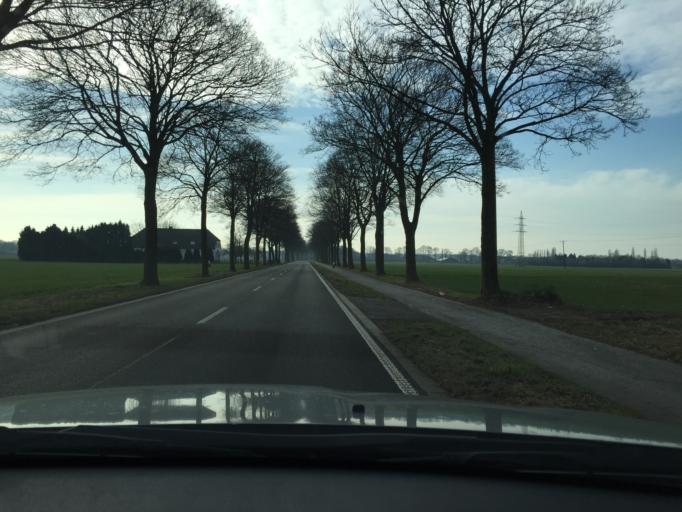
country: DE
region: North Rhine-Westphalia
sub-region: Regierungsbezirk Dusseldorf
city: Kleve
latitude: 51.7624
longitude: 6.1311
